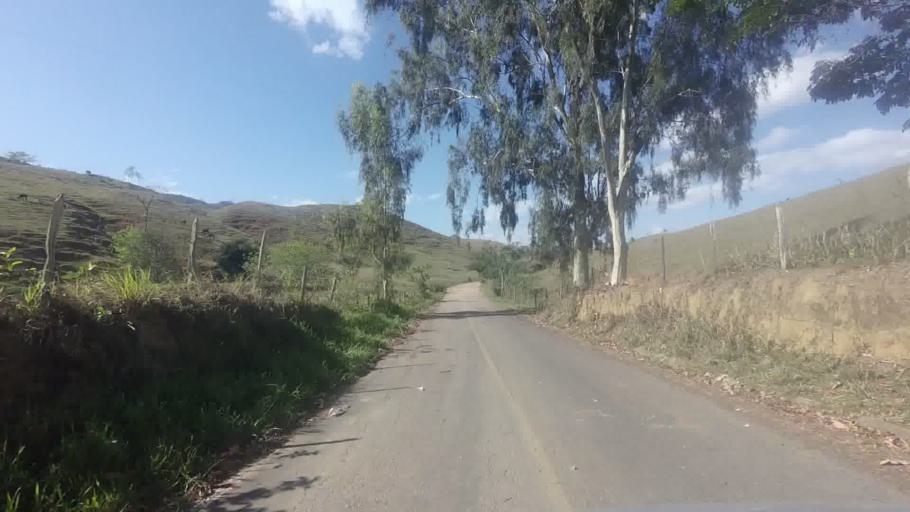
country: BR
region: Rio de Janeiro
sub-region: Bom Jesus Do Itabapoana
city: Bom Jesus do Itabapoana
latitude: -21.1112
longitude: -41.6494
